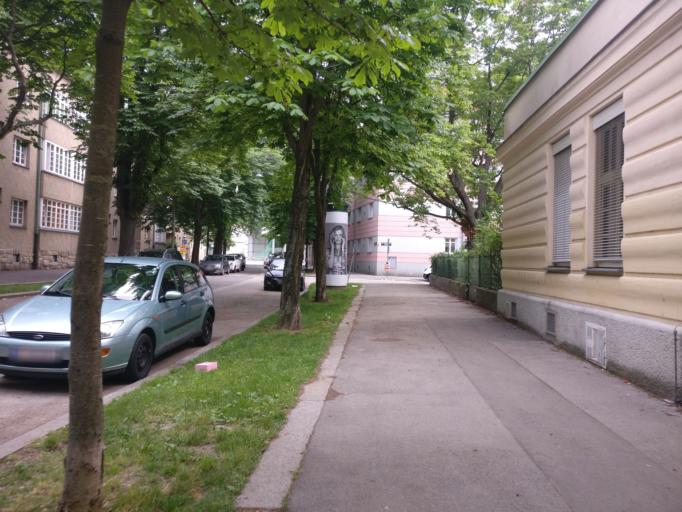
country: AT
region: Vienna
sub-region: Wien Stadt
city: Vienna
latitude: 48.1717
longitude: 16.3414
